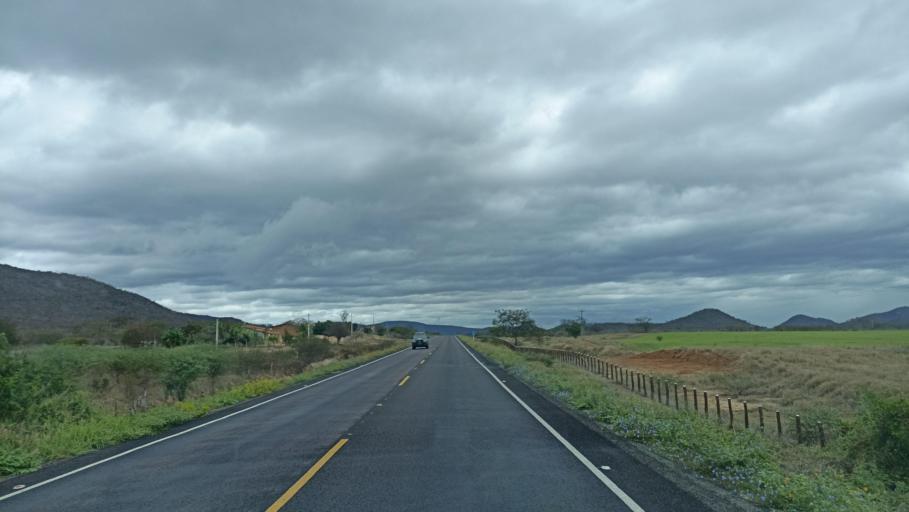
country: BR
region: Bahia
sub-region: Iacu
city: Iacu
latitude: -12.8943
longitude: -40.3985
